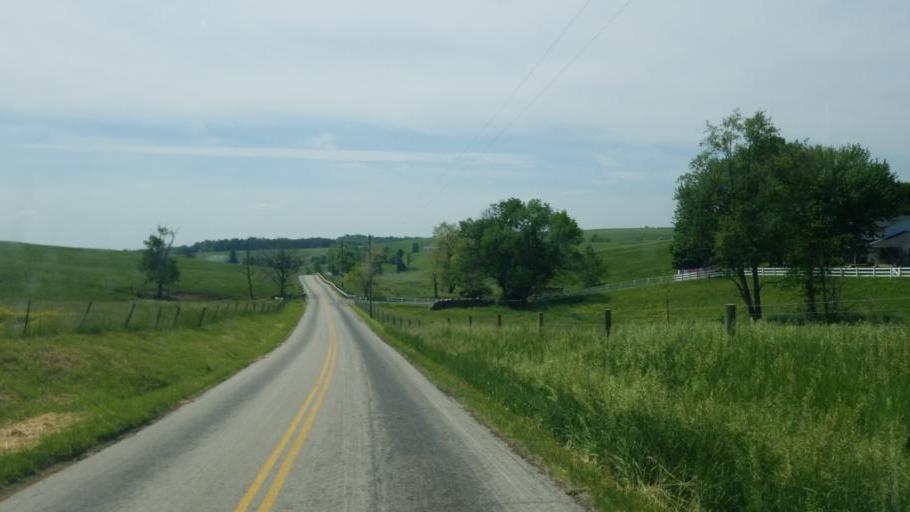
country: US
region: Ohio
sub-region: Tuscarawas County
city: Sugarcreek
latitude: 40.5152
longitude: -81.6860
